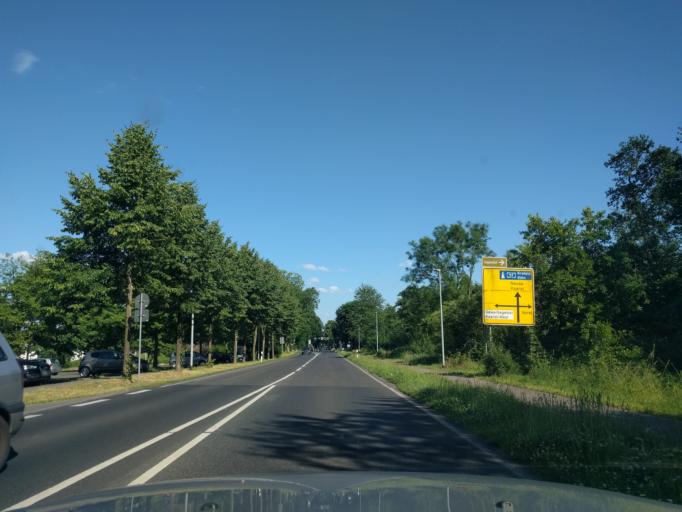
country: DE
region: North Rhine-Westphalia
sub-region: Regierungsbezirk Dusseldorf
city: Kaarst
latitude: 51.2269
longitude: 6.5947
